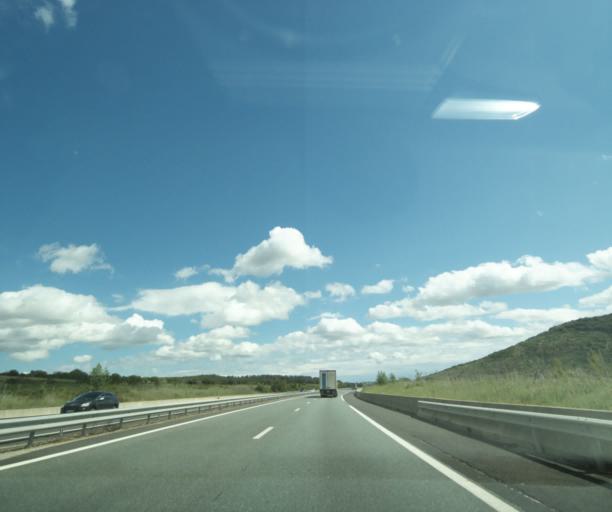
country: FR
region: Languedoc-Roussillon
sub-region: Departement de l'Herault
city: Nebian
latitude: 43.6741
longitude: 3.4238
